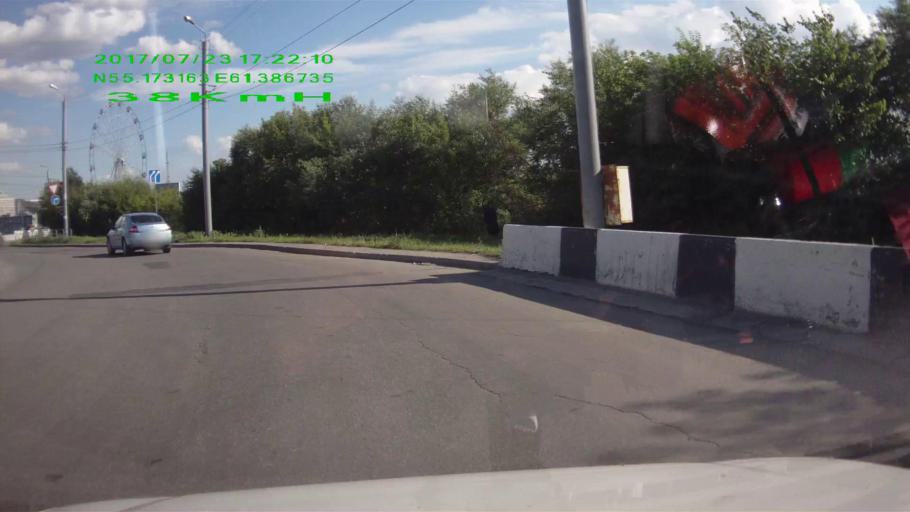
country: RU
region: Chelyabinsk
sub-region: Gorod Chelyabinsk
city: Chelyabinsk
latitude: 55.1729
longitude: 61.3871
